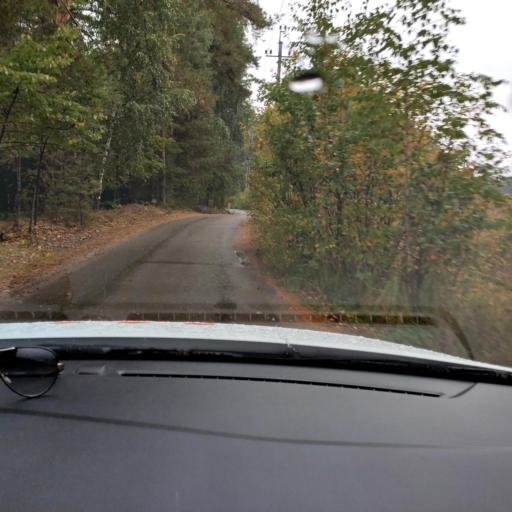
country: RU
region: Tatarstan
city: Verkhniy Uslon
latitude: 55.6418
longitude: 49.0188
